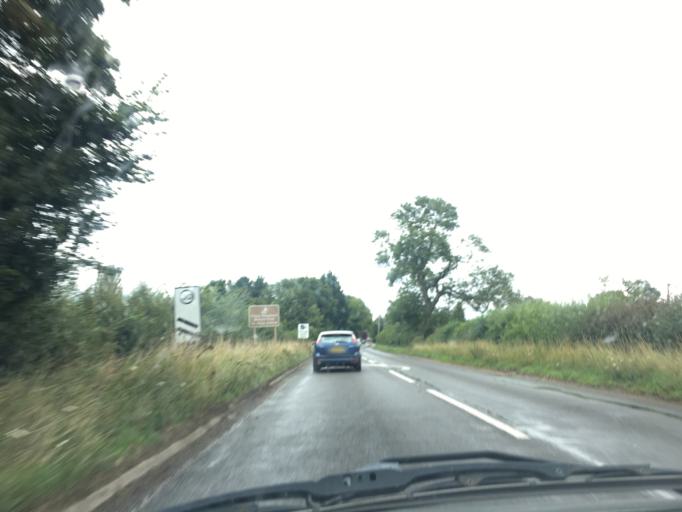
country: GB
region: England
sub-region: Leicestershire
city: Sapcote
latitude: 52.5176
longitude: -1.2978
